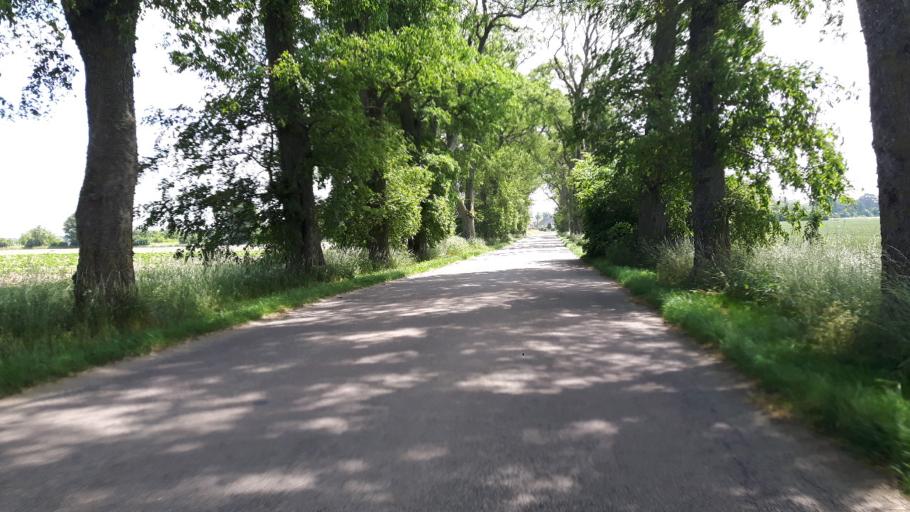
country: PL
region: Pomeranian Voivodeship
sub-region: Powiat wejherowski
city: Choczewo
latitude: 54.7386
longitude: 17.8216
